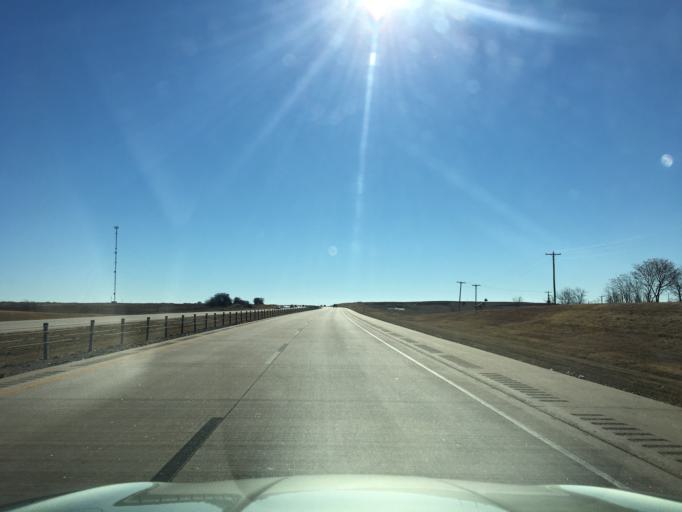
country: US
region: Oklahoma
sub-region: Kay County
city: Tonkawa
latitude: 36.5158
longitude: -97.3374
